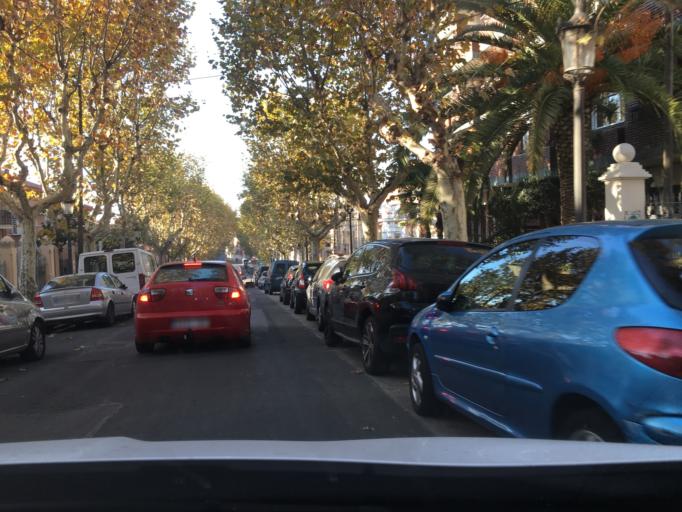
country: ES
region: Catalonia
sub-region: Provincia de Barcelona
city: Santa Coloma de Gramenet
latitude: 41.4532
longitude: 2.2115
